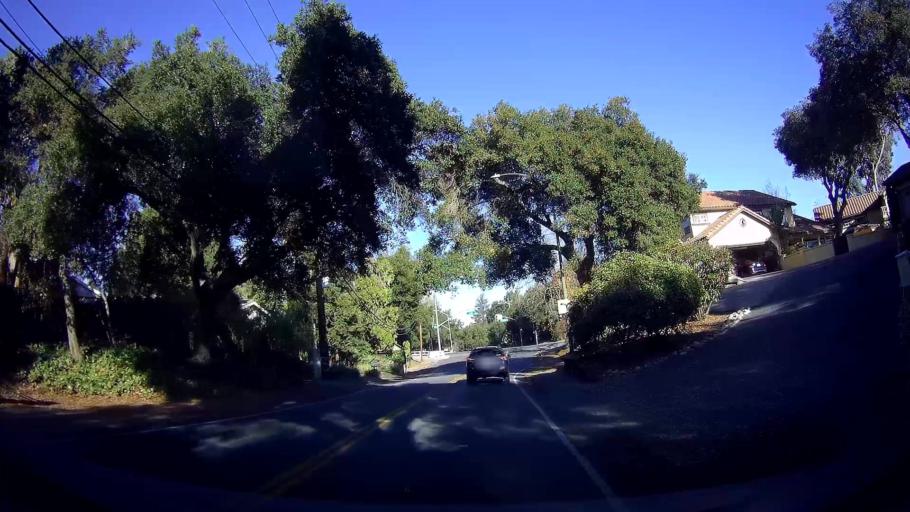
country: US
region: California
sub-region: Santa Clara County
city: Cambrian Park
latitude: 37.2821
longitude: -121.9231
